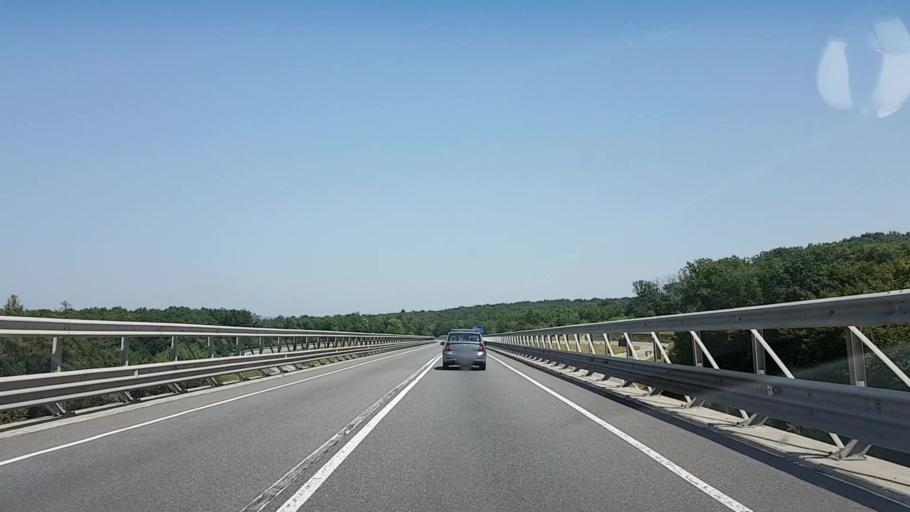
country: RO
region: Cluj
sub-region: Comuna Feleacu
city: Gheorghieni
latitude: 46.7281
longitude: 23.6569
